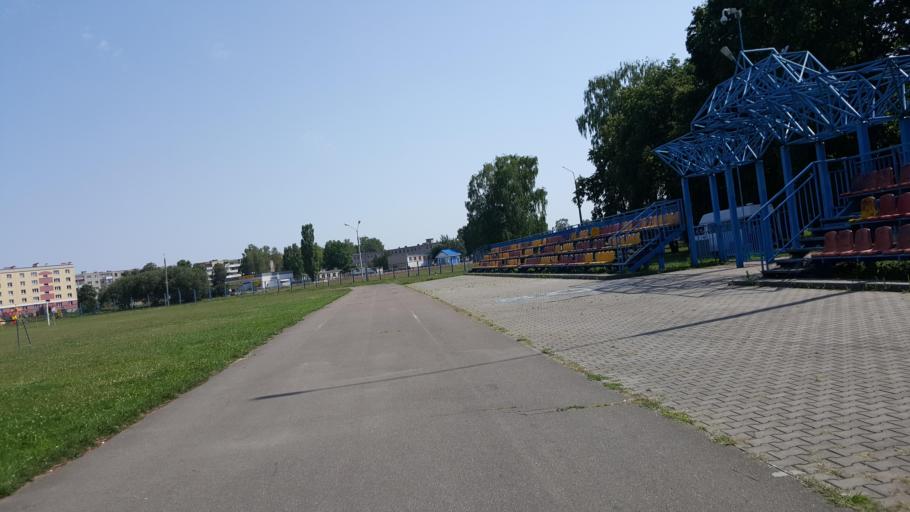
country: BY
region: Brest
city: Zhabinka
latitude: 52.1949
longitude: 24.0254
